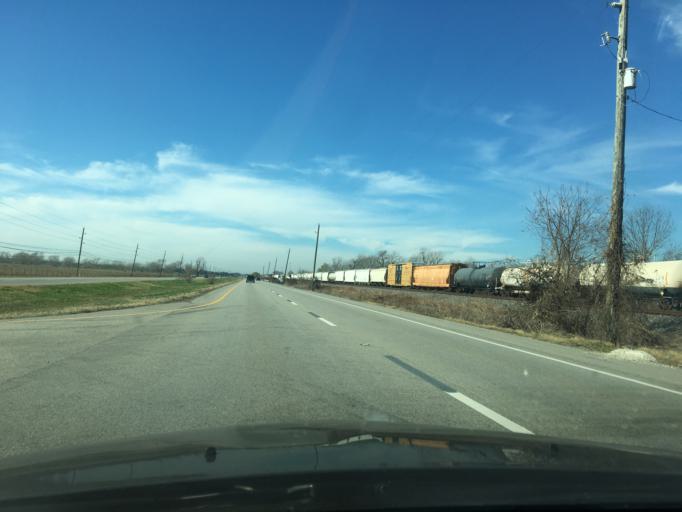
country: US
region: Texas
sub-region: Fort Bend County
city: New Territory
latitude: 29.6003
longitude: -95.6992
